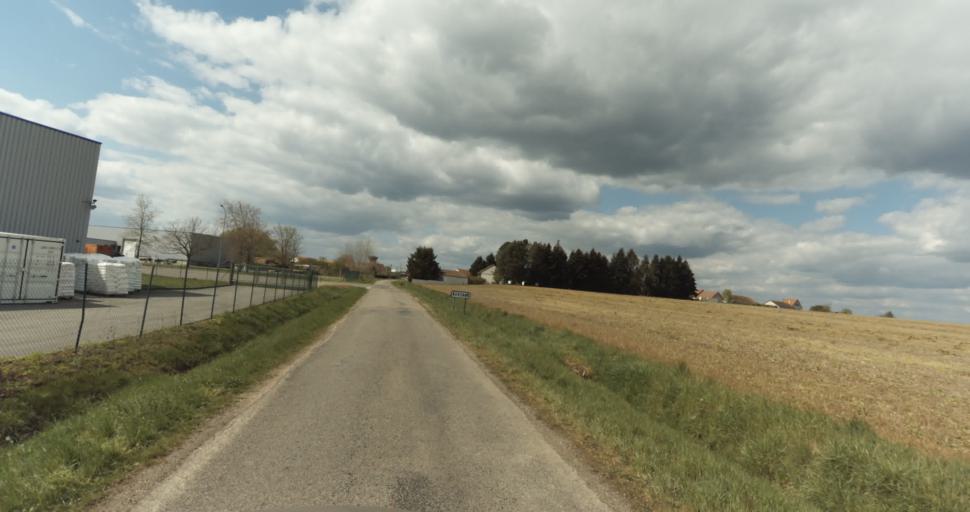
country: FR
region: Bourgogne
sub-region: Departement de la Cote-d'Or
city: Auxonne
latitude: 47.1784
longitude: 5.4076
